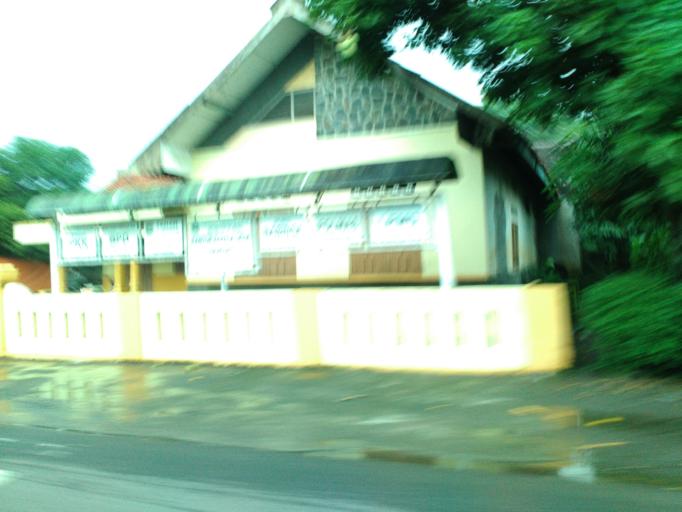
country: ID
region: Central Java
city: Ceper
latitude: -7.6530
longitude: 110.6892
